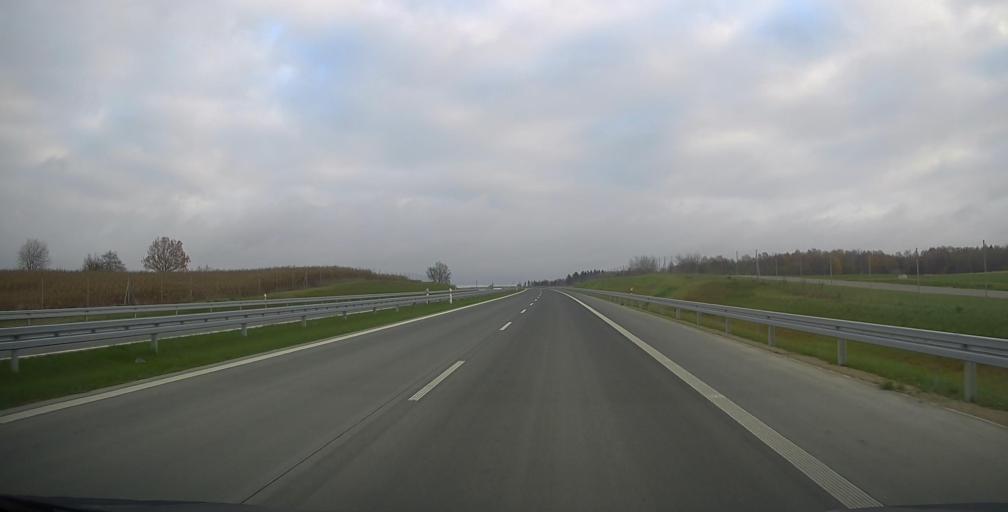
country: PL
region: Podlasie
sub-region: Powiat suwalski
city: Raczki
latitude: 53.9196
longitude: 22.7417
